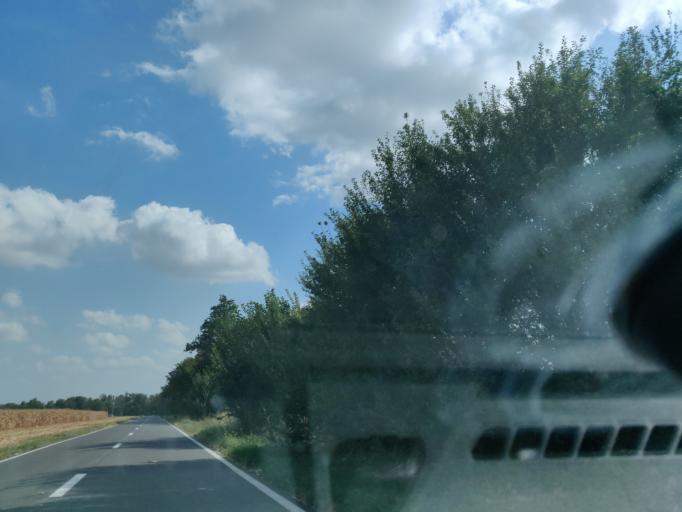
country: RO
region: Vrancea
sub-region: Comuna Maicanesti
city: Ramniceni
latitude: 45.4529
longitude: 27.3975
